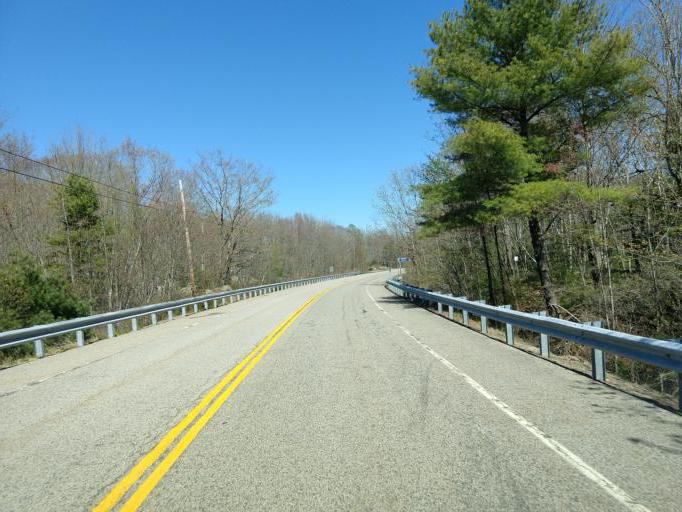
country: US
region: Maine
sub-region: York County
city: Biddeford
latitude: 43.4253
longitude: -70.3999
